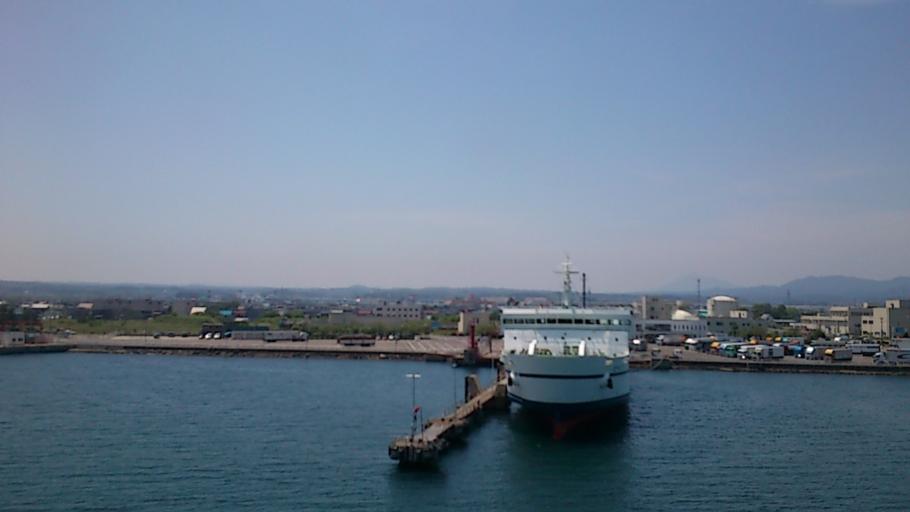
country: JP
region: Aomori
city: Aomori Shi
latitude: 40.8458
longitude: 140.7197
